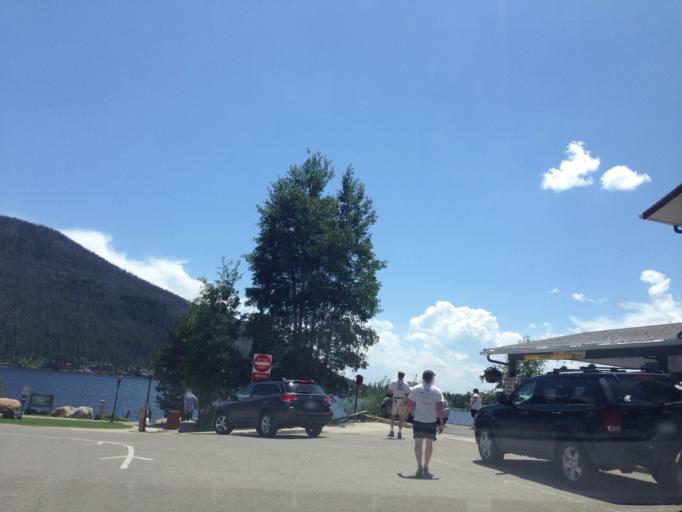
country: US
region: Colorado
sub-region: Grand County
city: Granby
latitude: 40.2512
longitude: -105.8199
